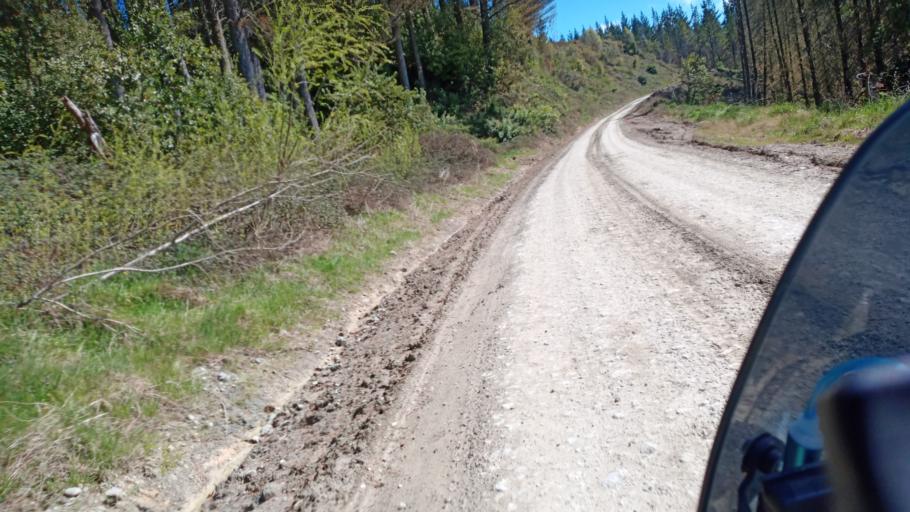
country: NZ
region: Gisborne
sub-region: Gisborne District
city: Gisborne
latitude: -38.8977
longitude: 177.8035
